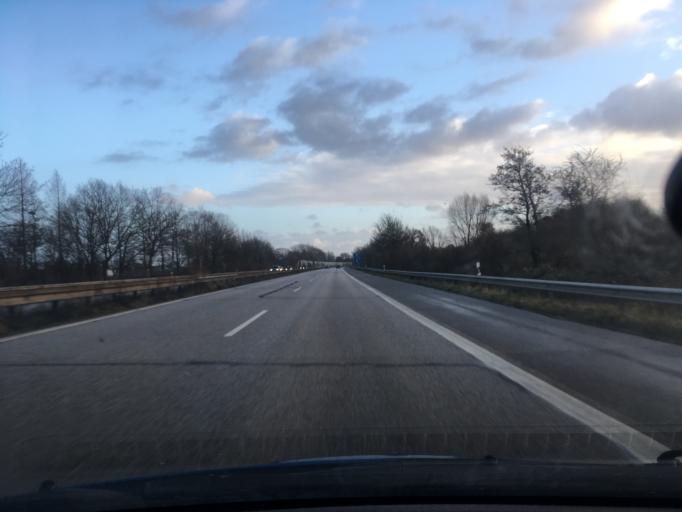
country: DE
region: Schleswig-Holstein
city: Rellingen
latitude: 53.6659
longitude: 9.8136
